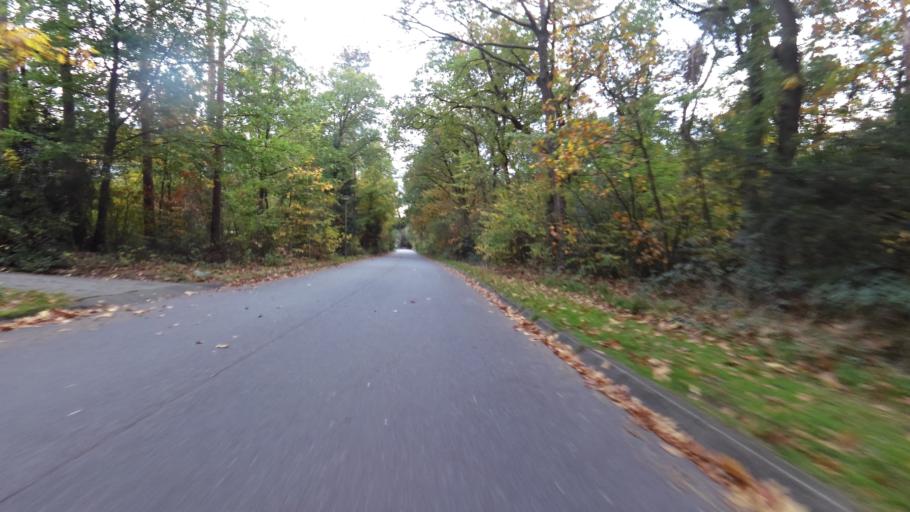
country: NL
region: Gelderland
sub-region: Gemeente Oldebroek
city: Oldebroek
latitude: 52.4105
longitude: 5.8808
